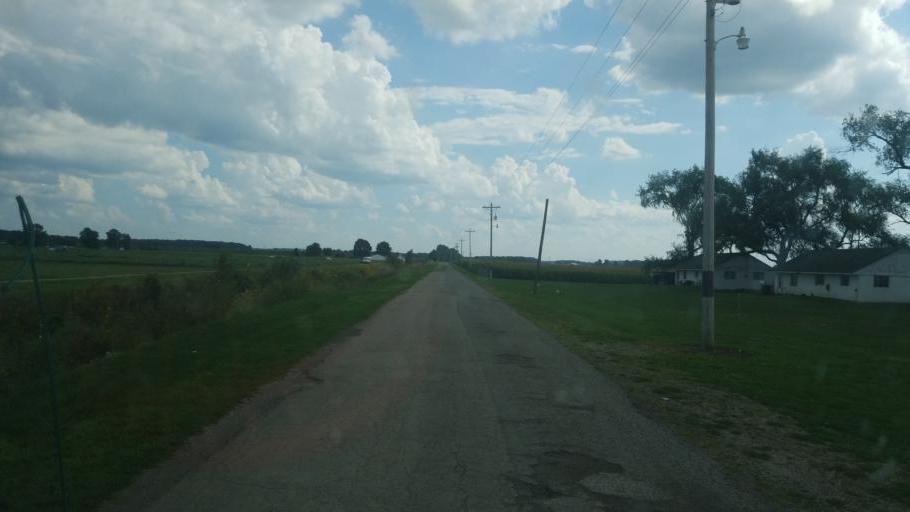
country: US
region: Ohio
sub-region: Huron County
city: Willard
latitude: 41.0017
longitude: -82.7392
